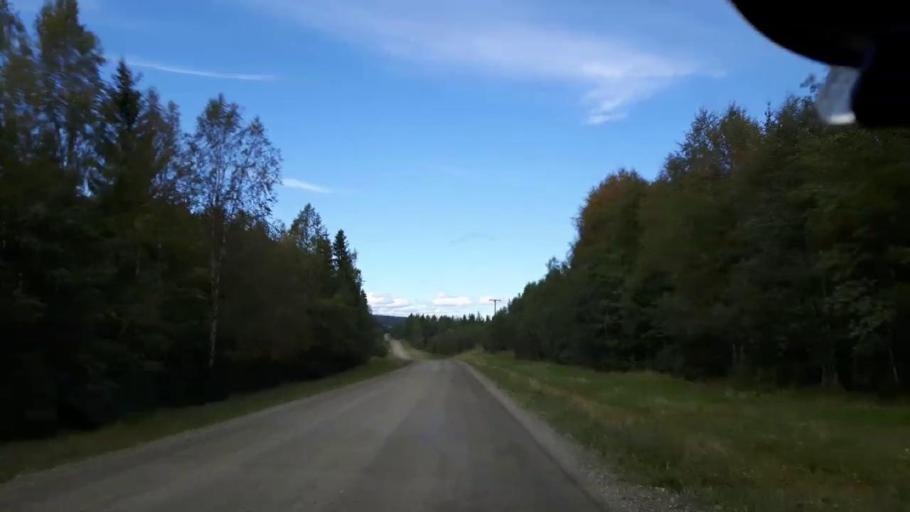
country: SE
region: Jaemtland
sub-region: Ragunda Kommun
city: Hammarstrand
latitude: 63.1247
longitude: 16.3282
